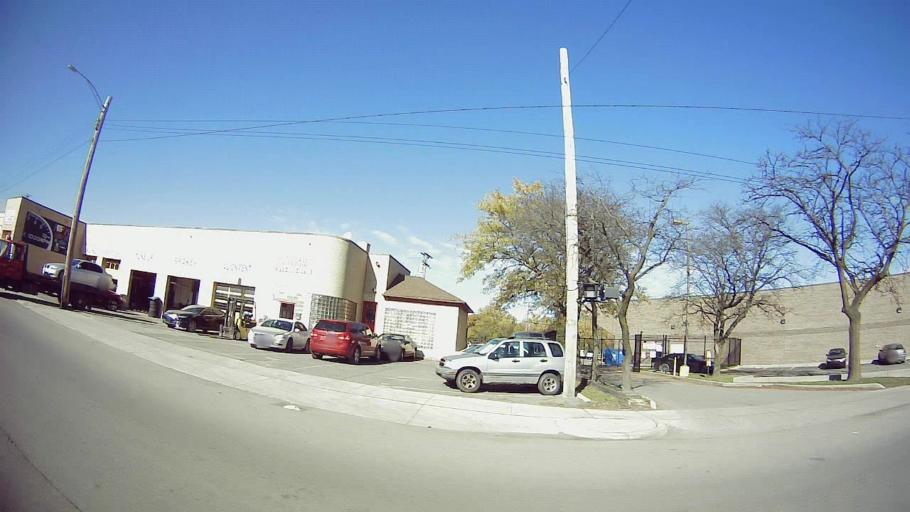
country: US
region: Michigan
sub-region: Wayne County
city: Dearborn
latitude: 42.3580
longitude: -83.2091
